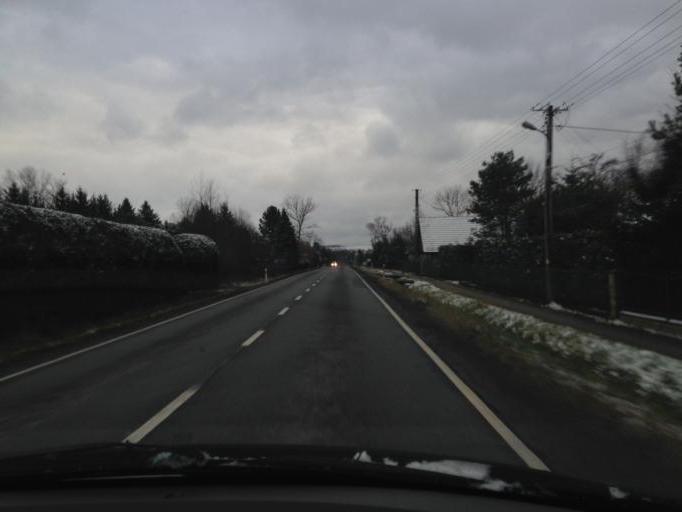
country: PL
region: Lesser Poland Voivodeship
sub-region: Powiat brzeski
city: Zlota
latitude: 49.8556
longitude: 20.6994
